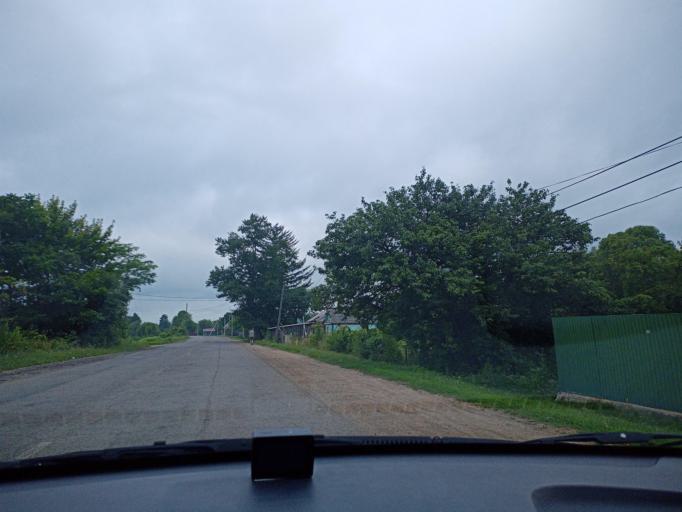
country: RU
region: Primorskiy
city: Novopokrovka
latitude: 45.8952
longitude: 134.8662
